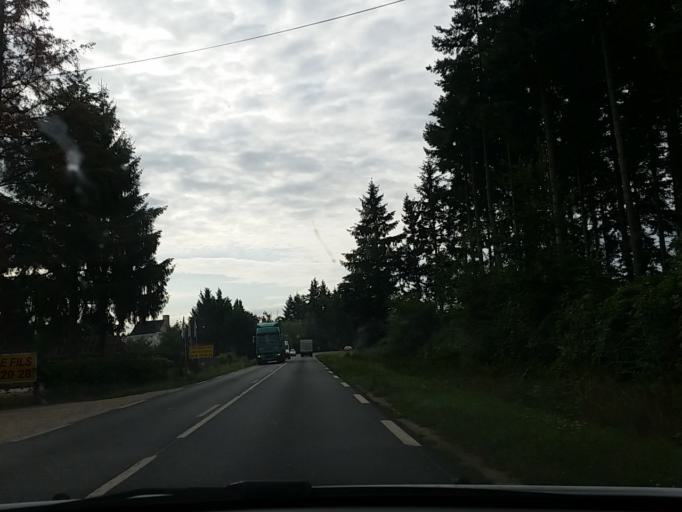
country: FR
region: Centre
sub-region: Departement du Loir-et-Cher
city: Cour-Cheverny
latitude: 47.5284
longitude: 1.4288
